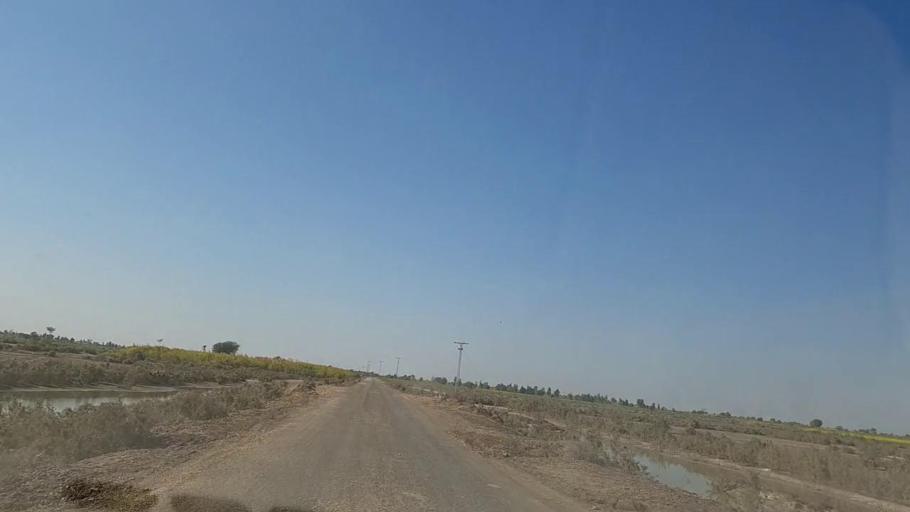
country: PK
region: Sindh
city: Digri
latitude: 25.1694
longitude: 69.0206
